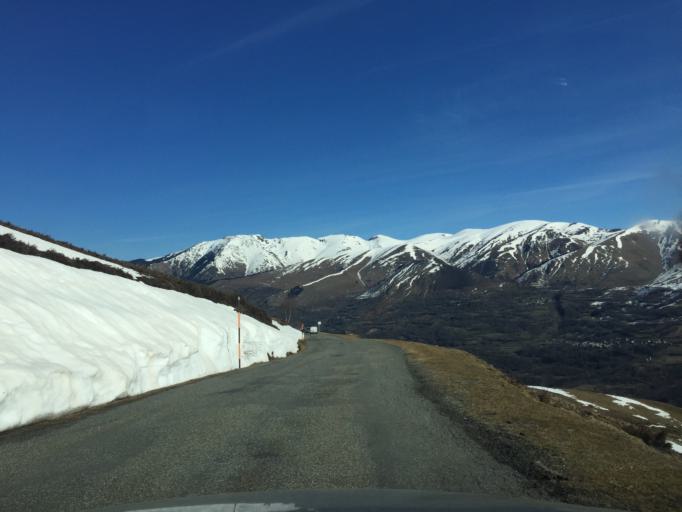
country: FR
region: Midi-Pyrenees
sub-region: Departement des Hautes-Pyrenees
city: Saint-Lary-Soulan
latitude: 42.7977
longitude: 0.3859
